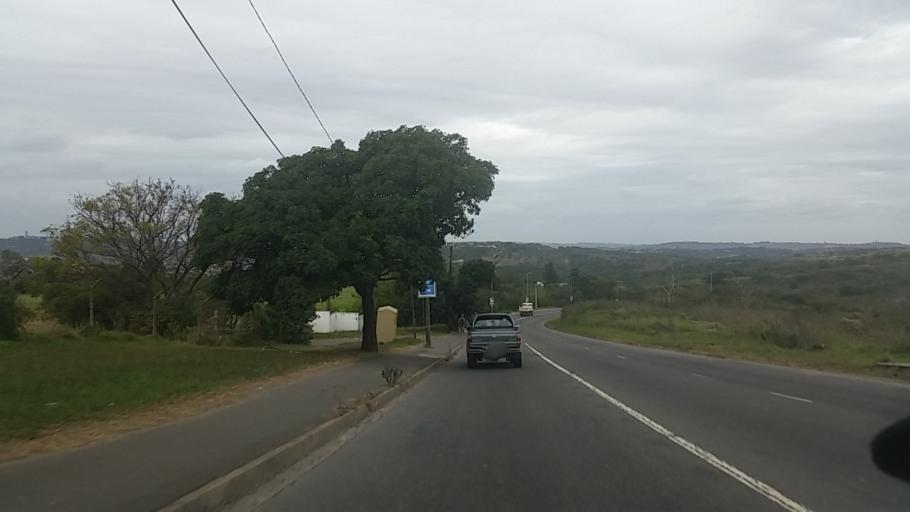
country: ZA
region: KwaZulu-Natal
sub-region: eThekwini Metropolitan Municipality
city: Berea
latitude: -29.8532
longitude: 30.9331
